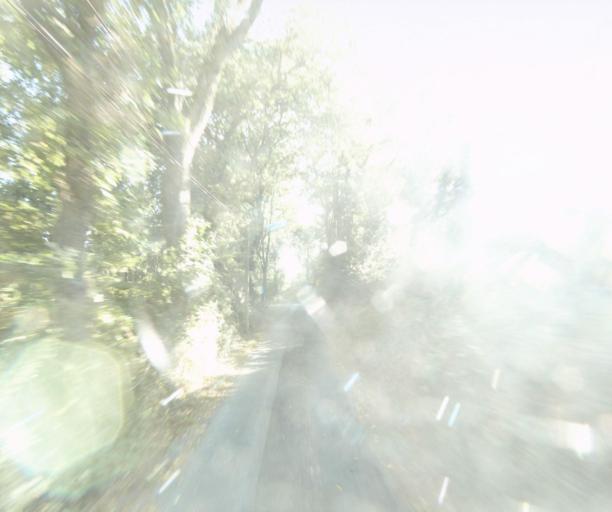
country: FR
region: Rhone-Alpes
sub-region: Departement du Rhone
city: Lentilly
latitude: 45.8021
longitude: 4.6590
